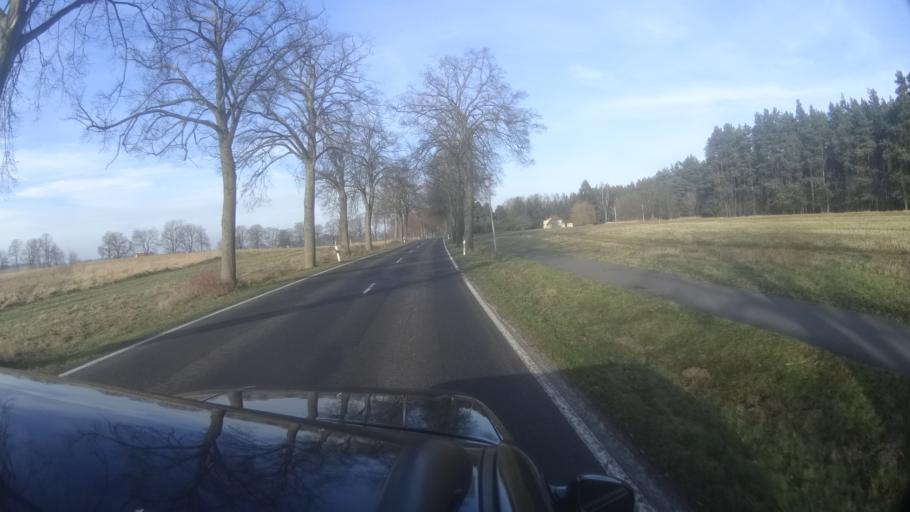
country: DE
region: Brandenburg
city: Kremmen
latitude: 52.8062
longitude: 13.0257
